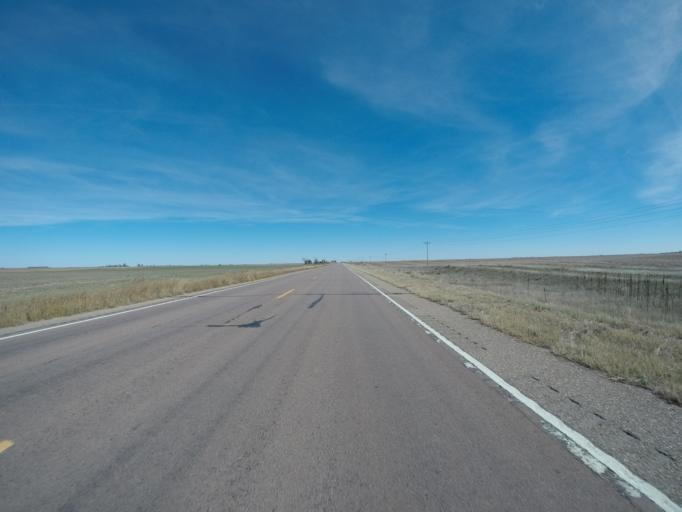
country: US
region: Colorado
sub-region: Yuma County
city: Yuma
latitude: 39.6559
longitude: -102.6666
